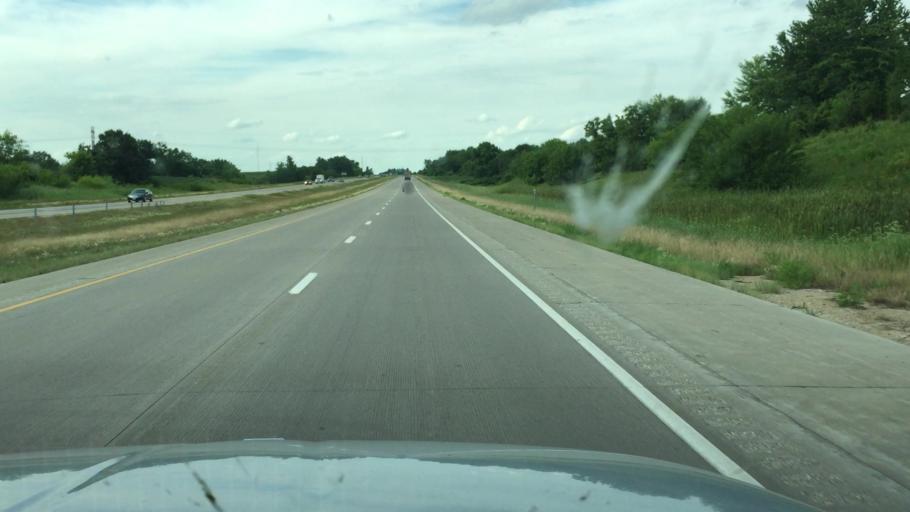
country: US
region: Iowa
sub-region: Scott County
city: Walcott
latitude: 41.5709
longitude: -90.6782
